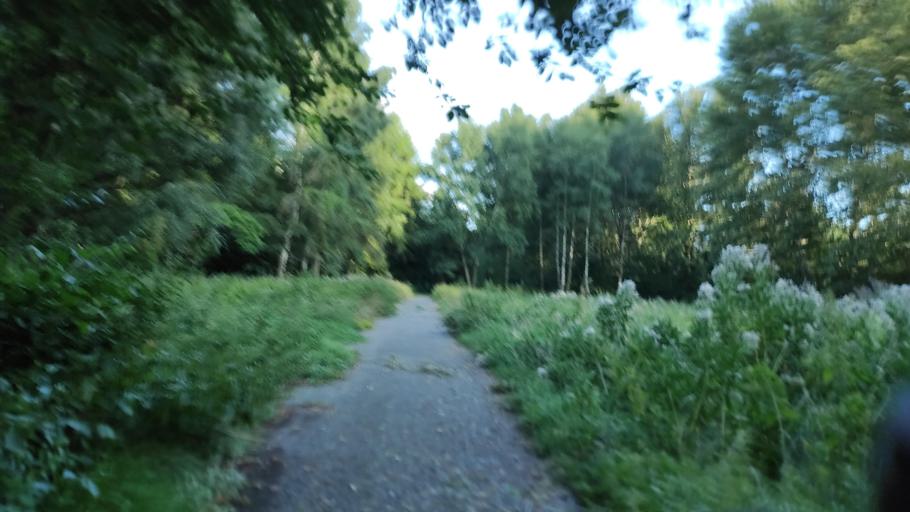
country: SK
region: Zilinsky
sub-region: Okres Liptovsky Mikulas
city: Liptovsky Mikulas
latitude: 49.0807
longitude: 19.5876
